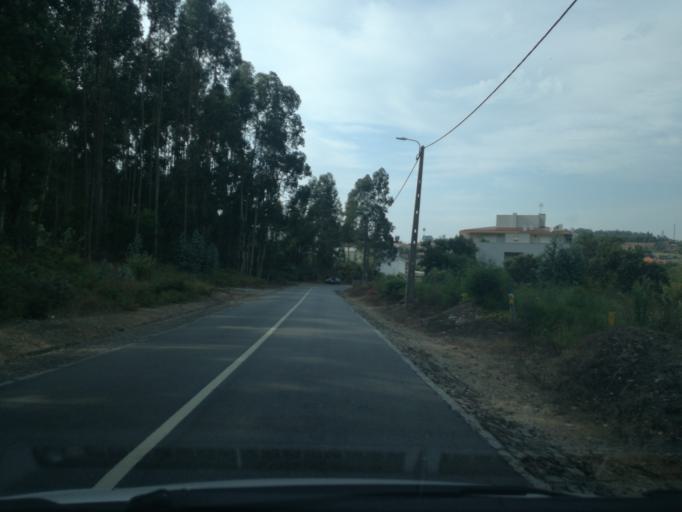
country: PT
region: Porto
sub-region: Vila Nova de Gaia
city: Sao Felix da Marinha
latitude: 41.0295
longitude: -8.6290
